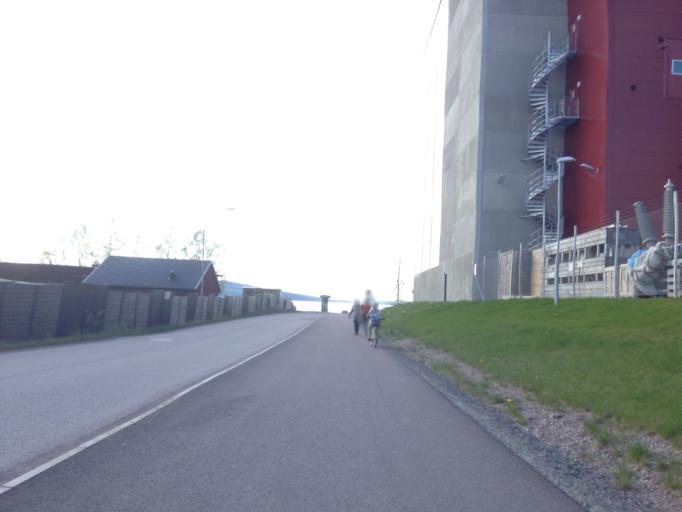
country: SE
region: Dalarna
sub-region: Ludvika Kommun
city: Ludvika
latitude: 60.1455
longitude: 15.1683
